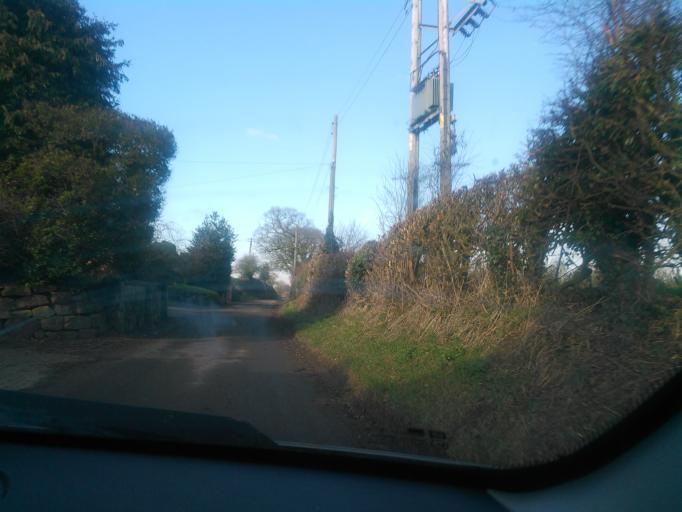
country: GB
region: England
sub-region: Shropshire
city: Wem
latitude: 52.8409
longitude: -2.6759
